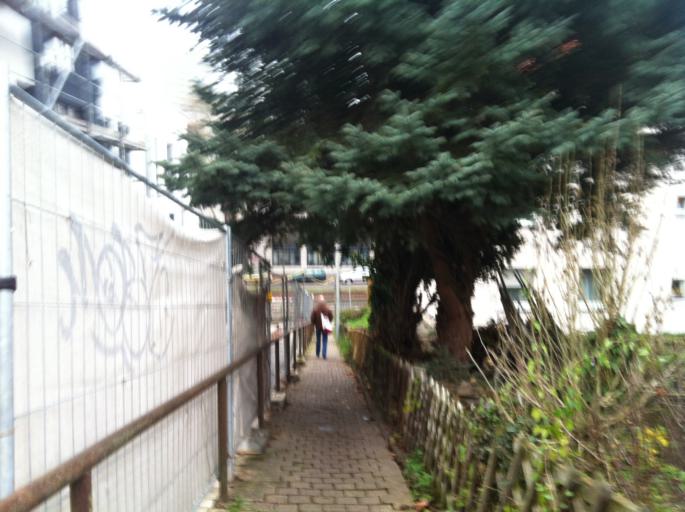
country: DE
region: Rheinland-Pfalz
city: Mainz
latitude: 49.9964
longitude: 8.2550
